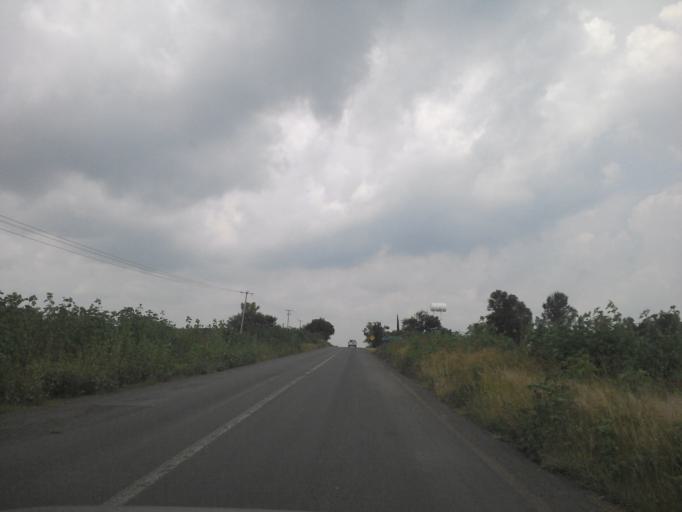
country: MX
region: Guanajuato
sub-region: San Francisco del Rincon
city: San Ignacio de Hidalgo
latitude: 20.8915
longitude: -101.9385
